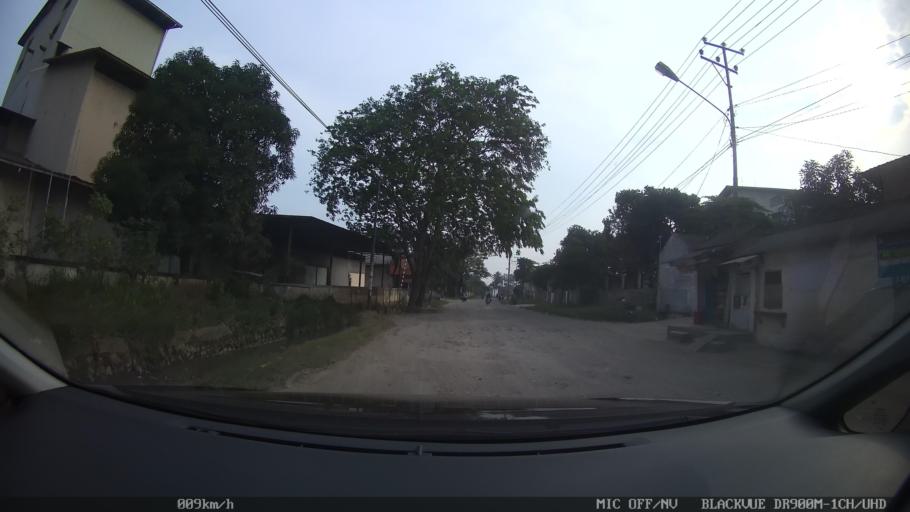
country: ID
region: Lampung
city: Panjang
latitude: -5.4500
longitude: 105.3089
